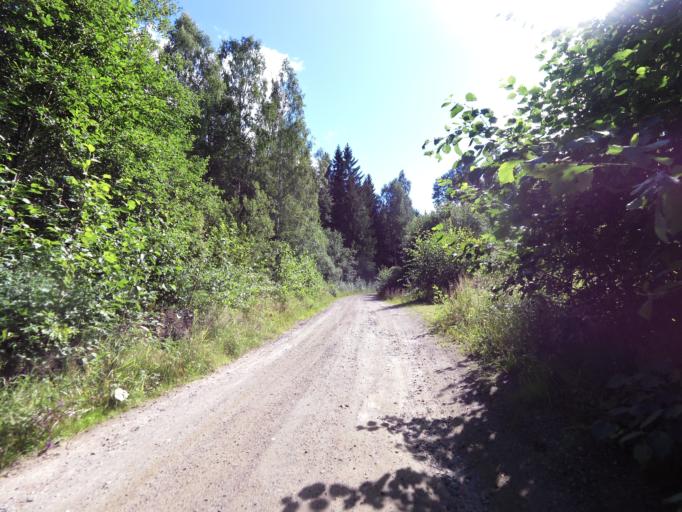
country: SE
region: Gaevleborg
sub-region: Hofors Kommun
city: Hofors
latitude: 60.5318
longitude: 16.2308
